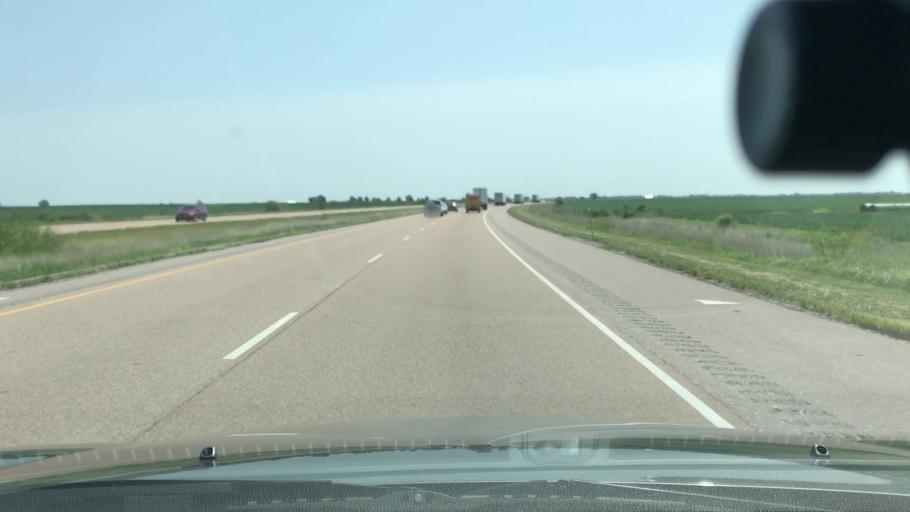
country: US
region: Illinois
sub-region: Washington County
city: Okawville
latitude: 38.4308
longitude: -89.4970
